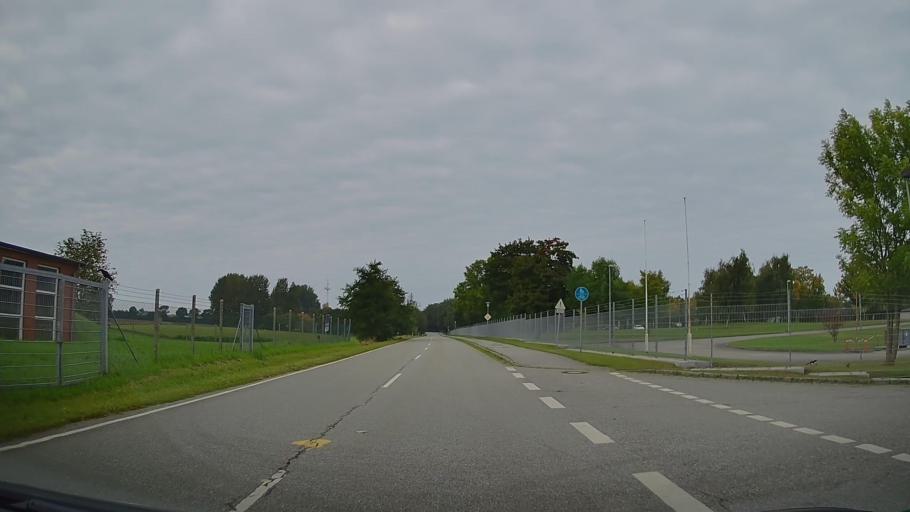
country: DE
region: Schleswig-Holstein
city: Panker
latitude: 54.3665
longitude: 10.5639
